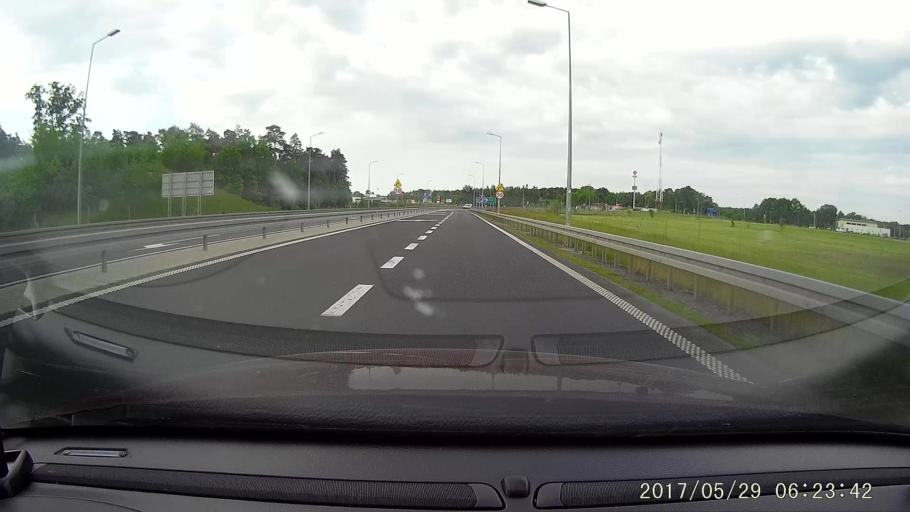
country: PL
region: Lower Silesian Voivodeship
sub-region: Powiat zgorzelecki
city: Wegliniec
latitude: 51.2166
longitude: 15.2442
